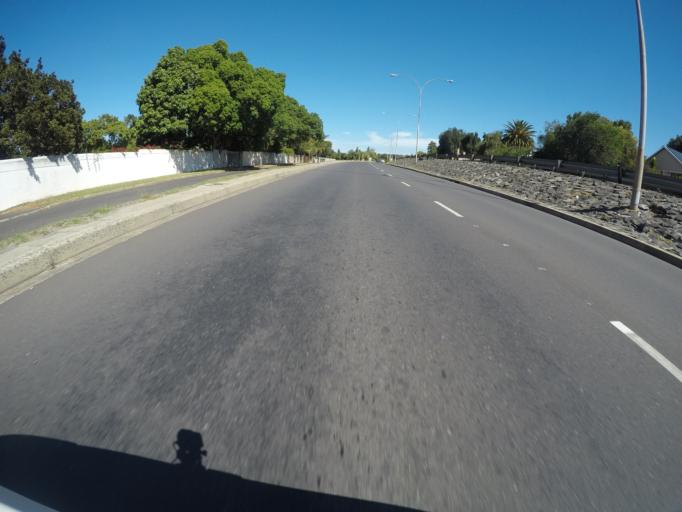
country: ZA
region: Western Cape
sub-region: City of Cape Town
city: Kraaifontein
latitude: -33.8412
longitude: 18.6481
